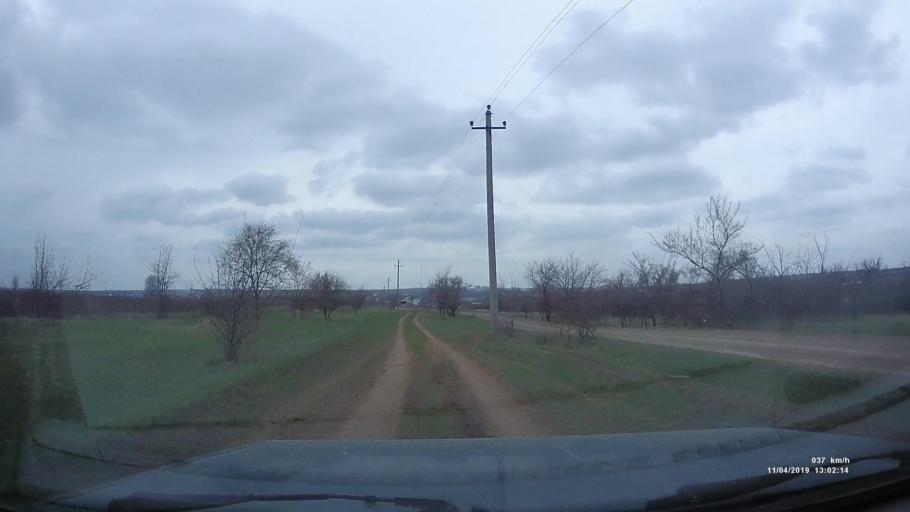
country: RU
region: Rostov
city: Staraya Stanitsa
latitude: 48.2876
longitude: 40.3599
